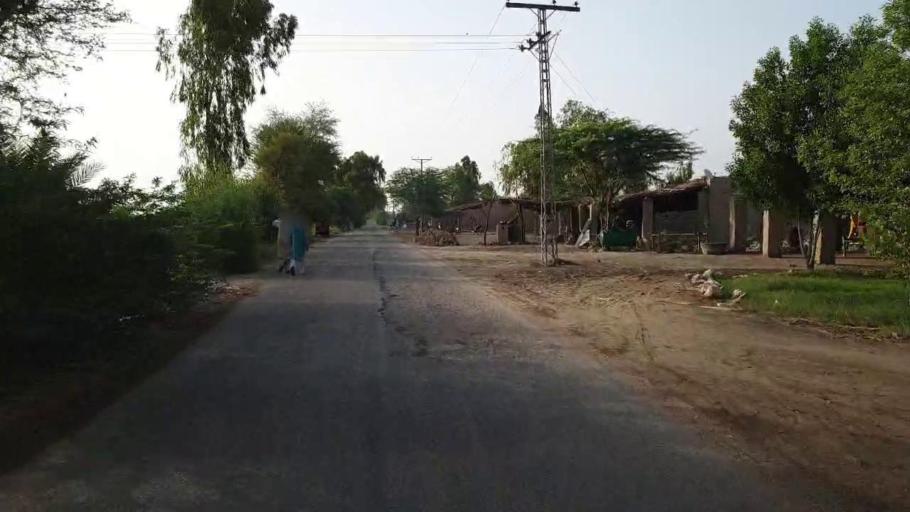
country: PK
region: Sindh
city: Bozdar
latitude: 27.1102
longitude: 68.9598
